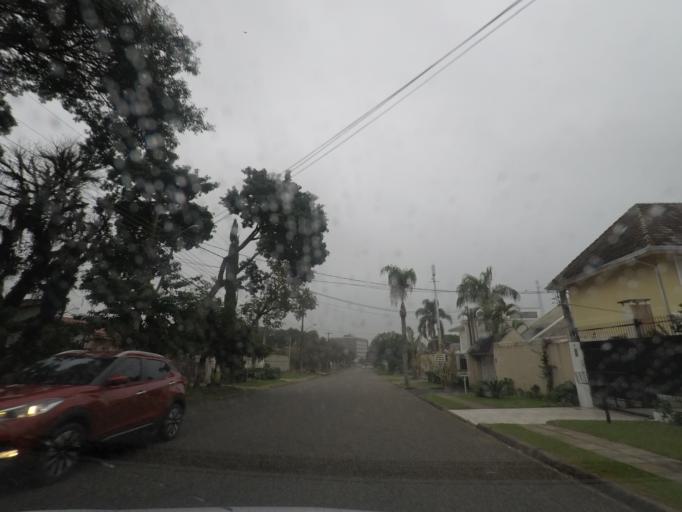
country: BR
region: Parana
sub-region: Curitiba
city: Curitiba
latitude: -25.4557
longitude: -49.2438
